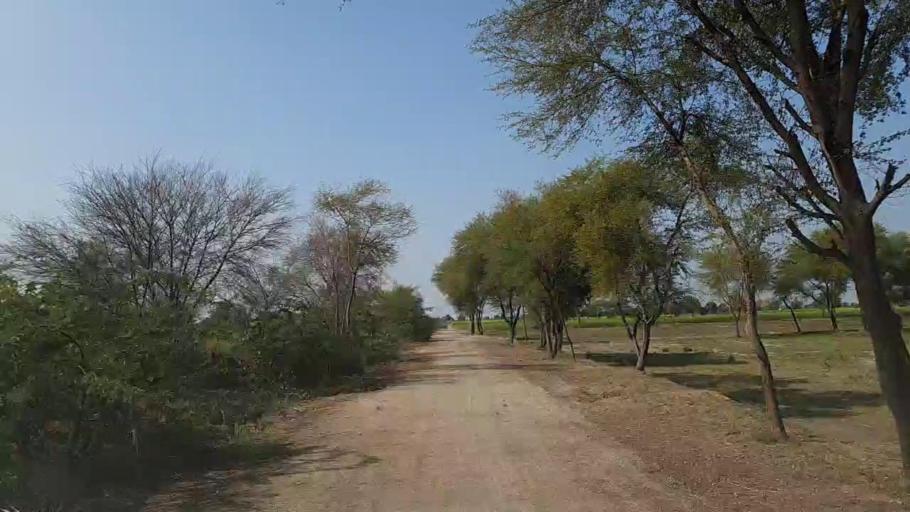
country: PK
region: Sindh
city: Nawabshah
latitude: 26.2948
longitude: 68.4760
